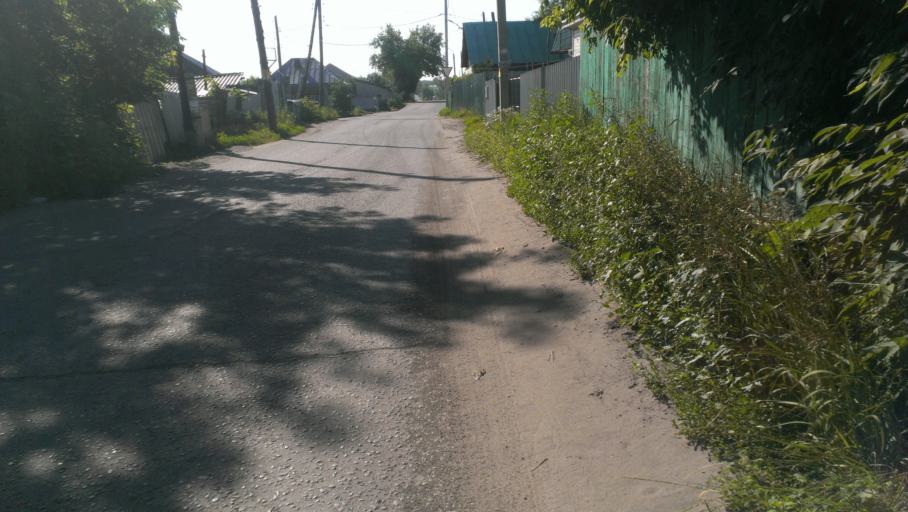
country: RU
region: Altai Krai
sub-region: Gorod Barnaulskiy
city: Barnaul
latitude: 53.3559
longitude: 83.7490
